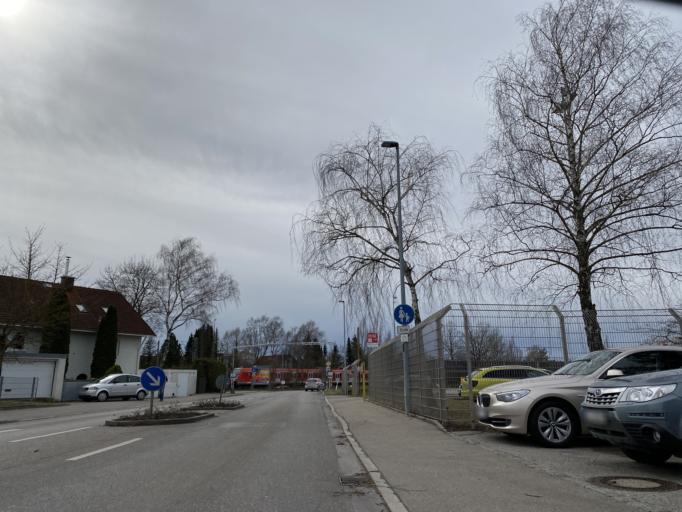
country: DE
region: Bavaria
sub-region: Upper Bavaria
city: Schongeising
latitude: 48.1598
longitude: 11.2214
